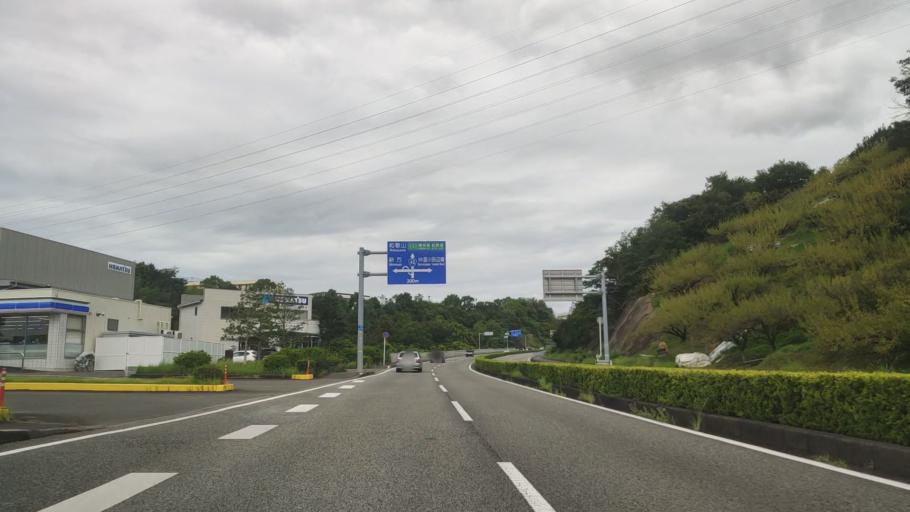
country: JP
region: Wakayama
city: Tanabe
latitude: 33.7285
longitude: 135.4010
